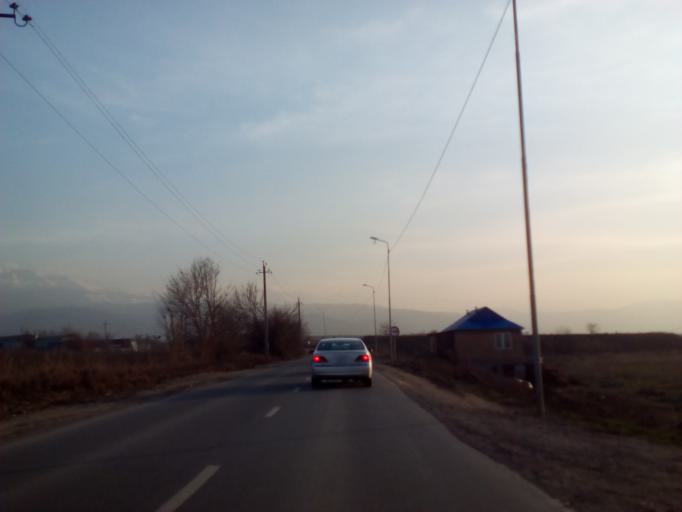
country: KZ
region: Almaty Oblysy
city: Burunday
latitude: 43.2354
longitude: 76.7415
